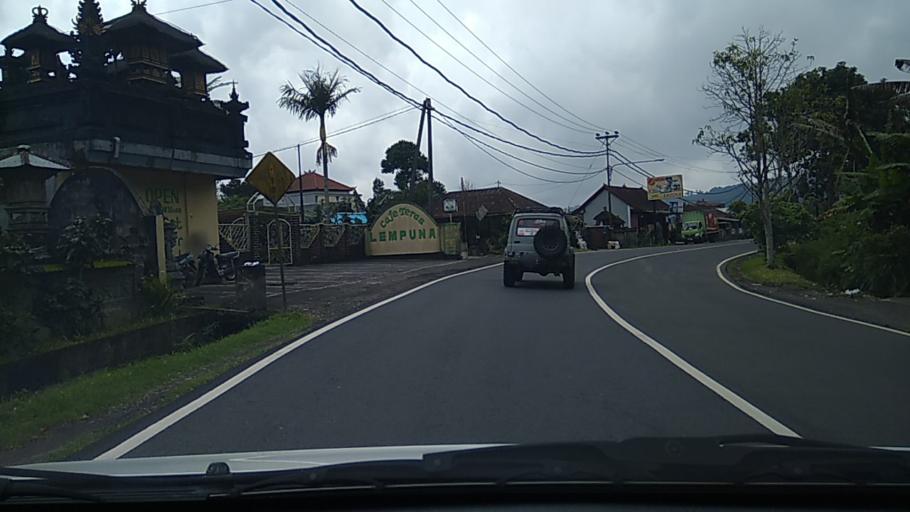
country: ID
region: Bali
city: Munduk
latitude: -8.2559
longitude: 115.1597
